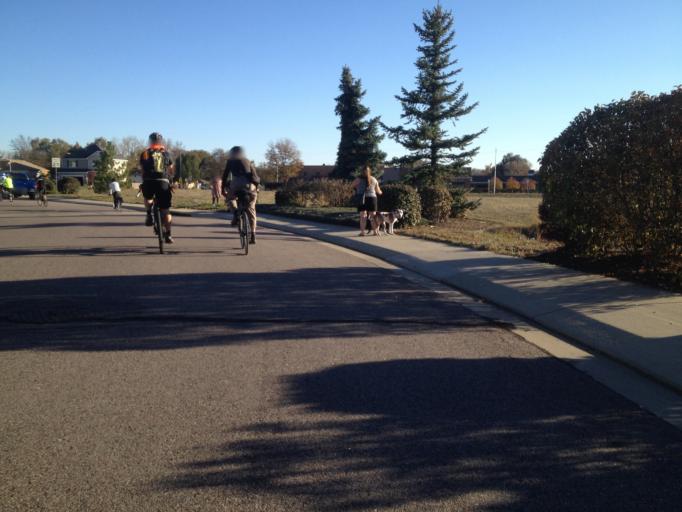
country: US
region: Colorado
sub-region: Boulder County
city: Longmont
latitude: 40.1845
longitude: -105.1152
